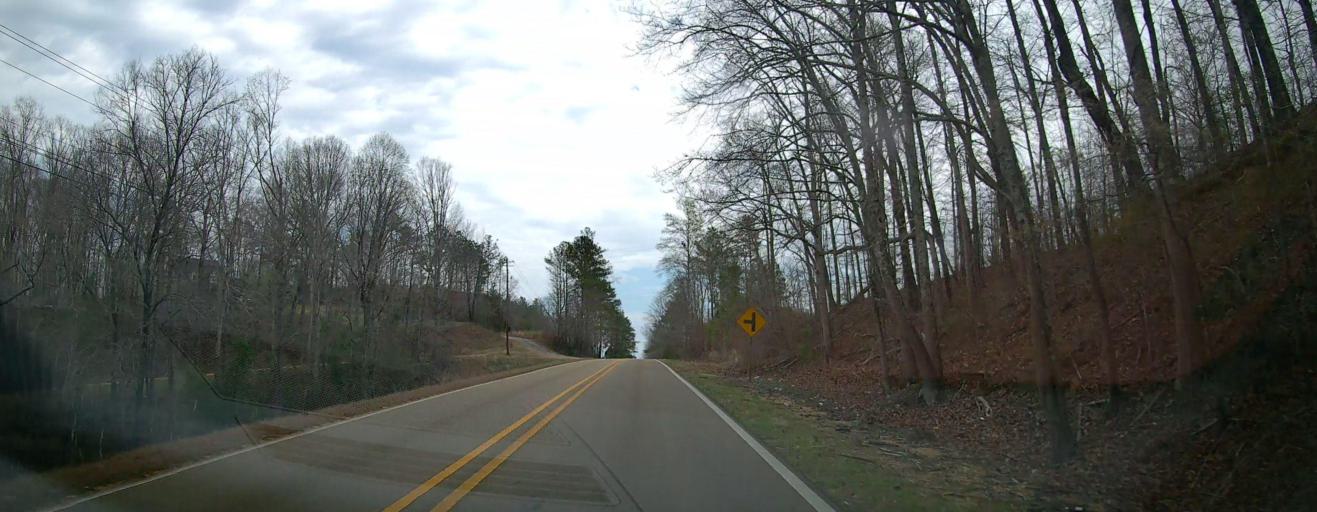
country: US
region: Mississippi
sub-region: Itawamba County
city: Fulton
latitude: 34.2478
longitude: -88.2951
